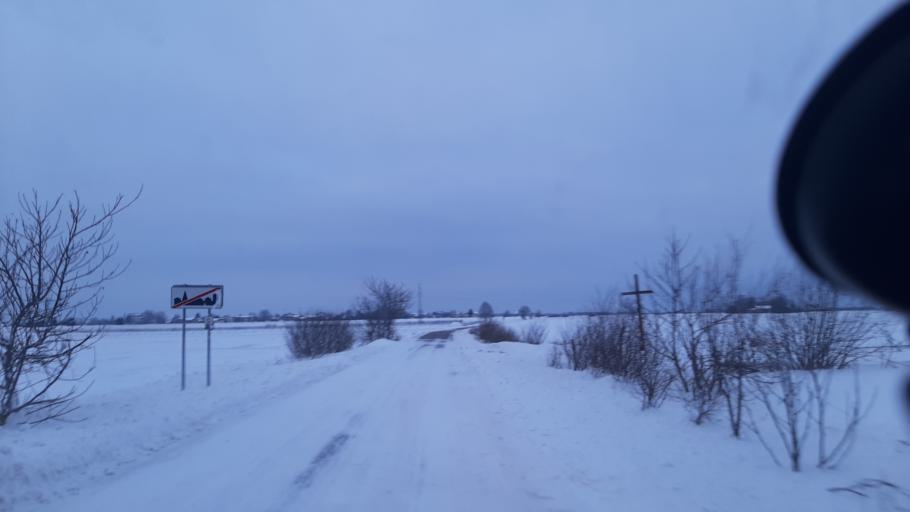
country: PL
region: Lublin Voivodeship
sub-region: Powiat lubelski
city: Jastkow
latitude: 51.3468
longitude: 22.4089
